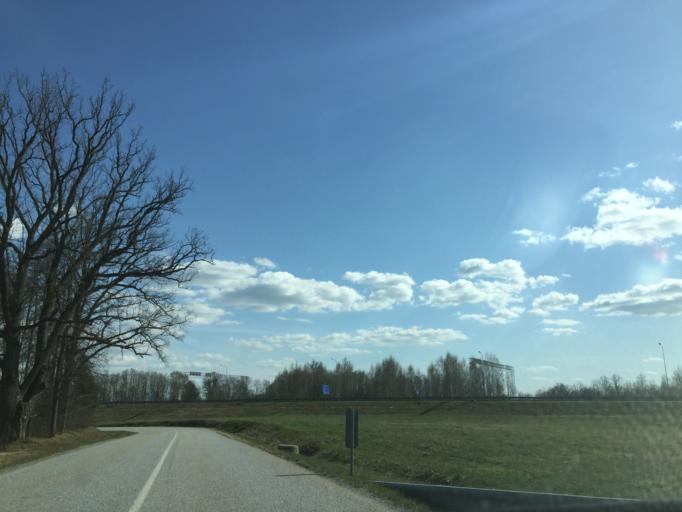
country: LV
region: Kegums
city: Kegums
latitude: 56.8252
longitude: 24.7607
